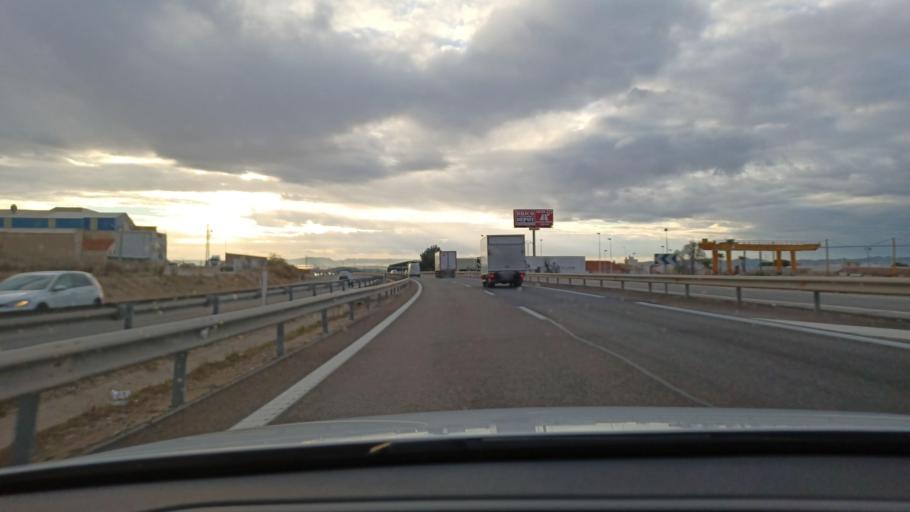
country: ES
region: Valencia
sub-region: Provincia de Alicante
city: Novelda
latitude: 38.4092
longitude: -0.7776
